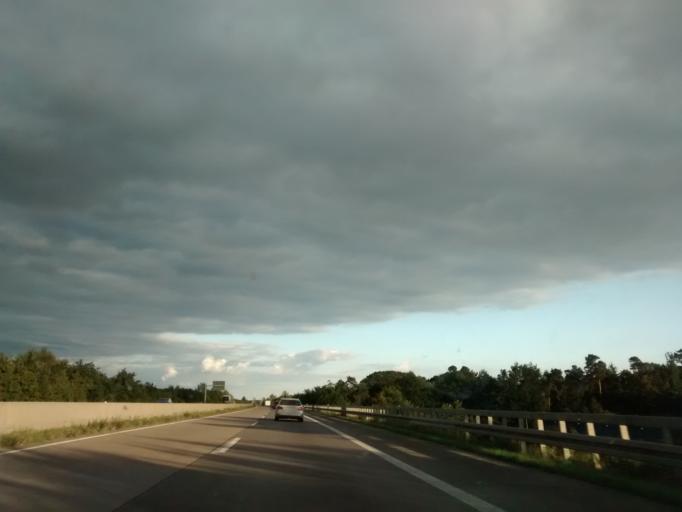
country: DE
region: North Rhine-Westphalia
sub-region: Regierungsbezirk Munster
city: Rheine
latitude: 52.3172
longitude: 7.4461
